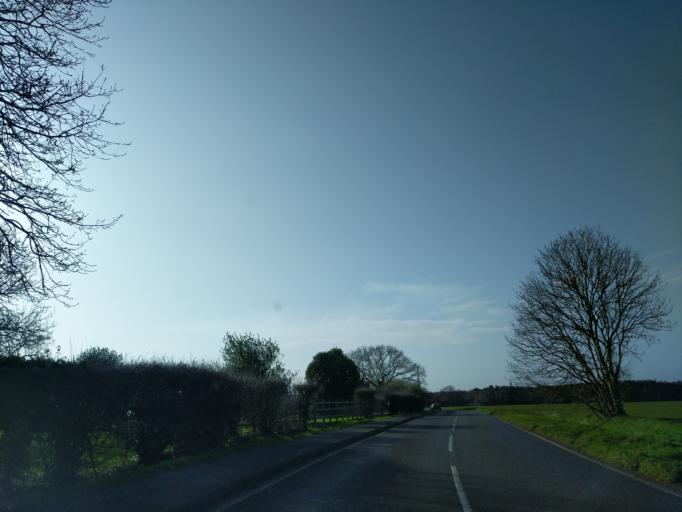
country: GB
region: England
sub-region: Cambridgeshire
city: Hemingford Grey
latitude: 52.3126
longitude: -0.0735
